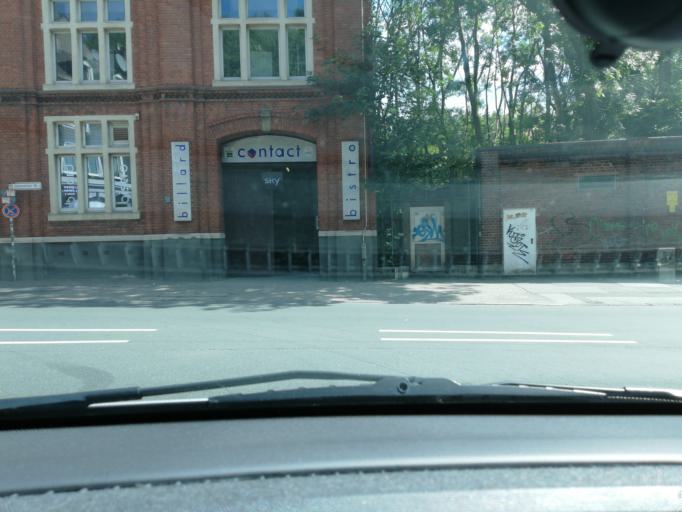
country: DE
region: North Rhine-Westphalia
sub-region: Regierungsbezirk Dusseldorf
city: Wuppertal
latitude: 51.2685
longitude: 7.1483
